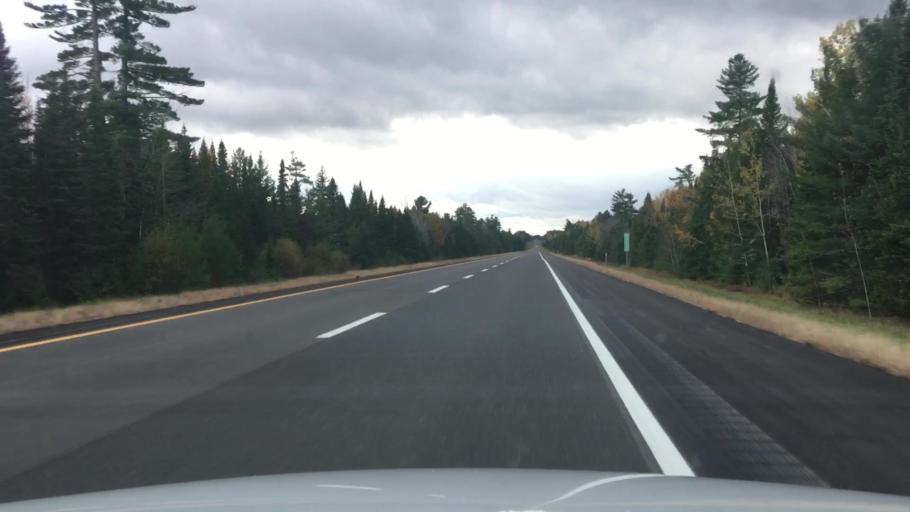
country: US
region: Maine
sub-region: Penobscot County
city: Patten
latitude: 46.0762
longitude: -68.2184
